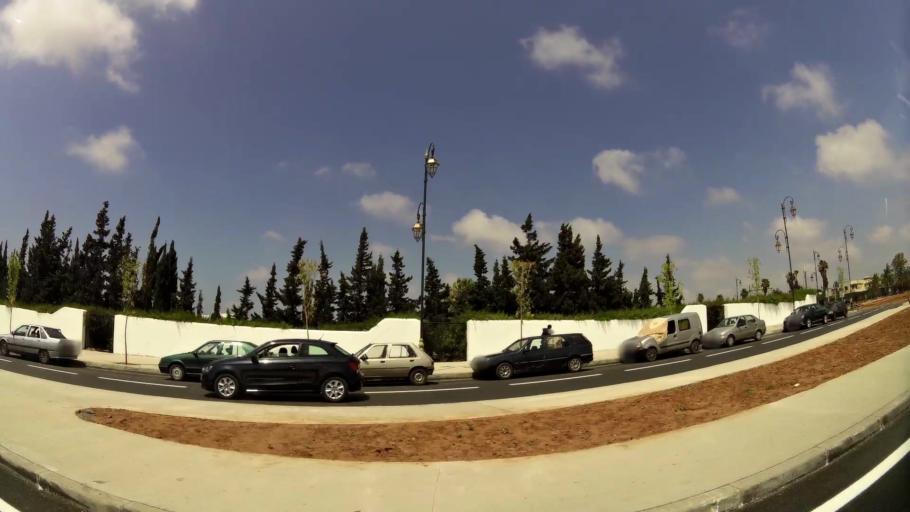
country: MA
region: Rabat-Sale-Zemmour-Zaer
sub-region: Skhirate-Temara
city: Temara
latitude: 33.9667
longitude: -6.8702
